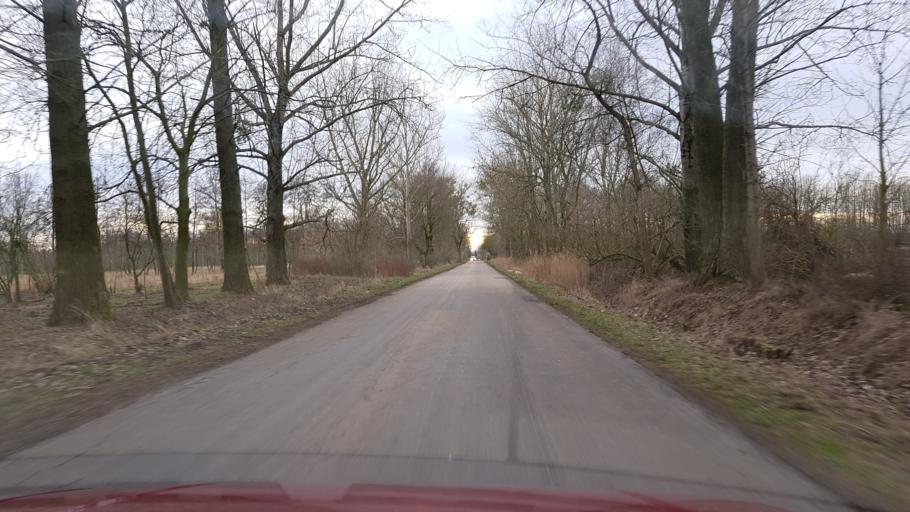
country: PL
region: West Pomeranian Voivodeship
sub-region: Powiat policki
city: Police
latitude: 53.5756
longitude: 14.5205
